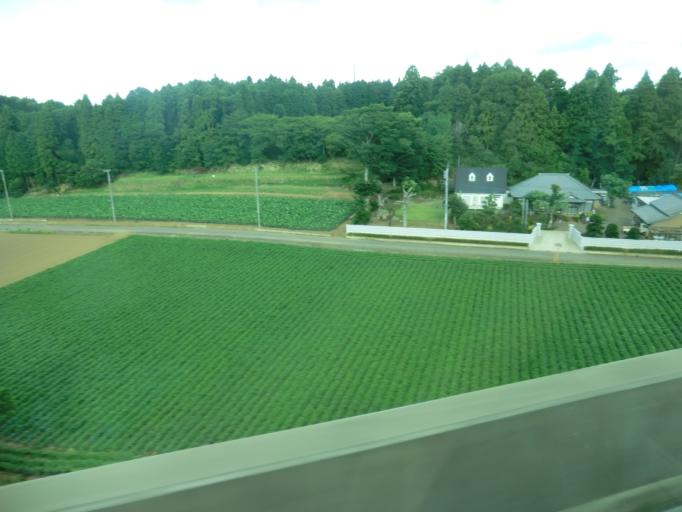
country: JP
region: Chiba
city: Narita
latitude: 35.8244
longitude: 140.3867
